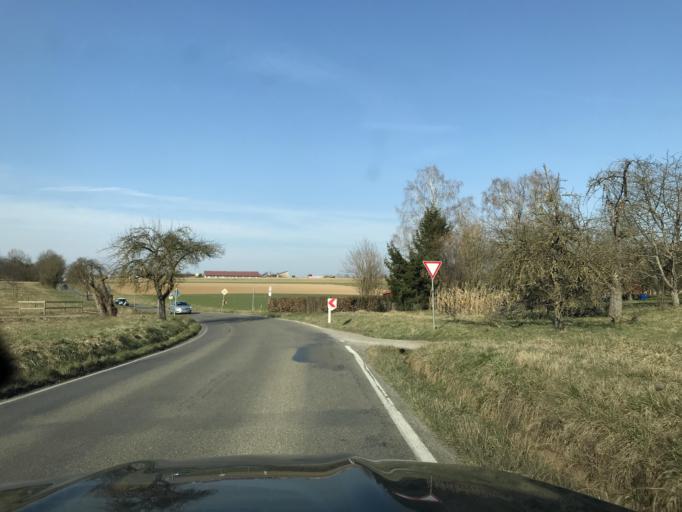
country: DE
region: Baden-Wuerttemberg
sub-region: Regierungsbezirk Stuttgart
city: Schwaikheim
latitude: 48.8798
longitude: 9.3620
